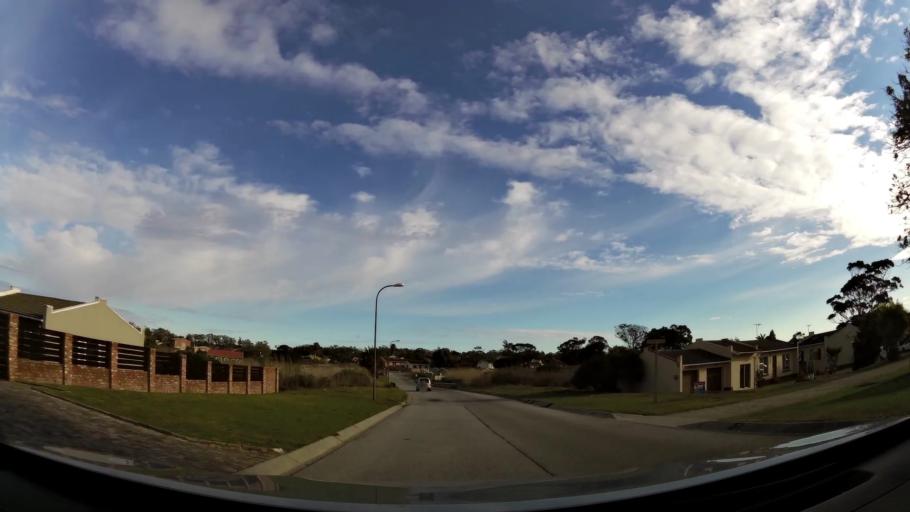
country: ZA
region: Eastern Cape
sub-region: Nelson Mandela Bay Metropolitan Municipality
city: Port Elizabeth
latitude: -33.9624
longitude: 25.4767
